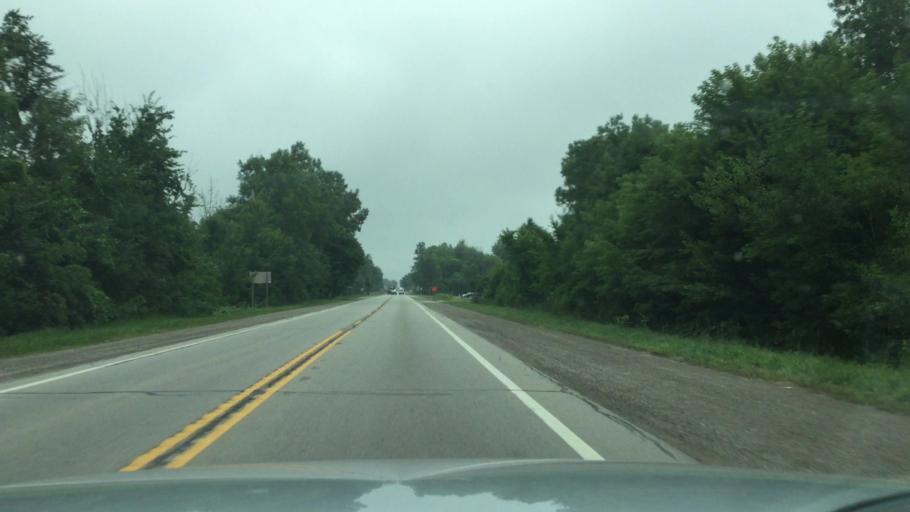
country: US
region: Michigan
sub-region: Shiawassee County
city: Durand
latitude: 42.9681
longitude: -83.9288
